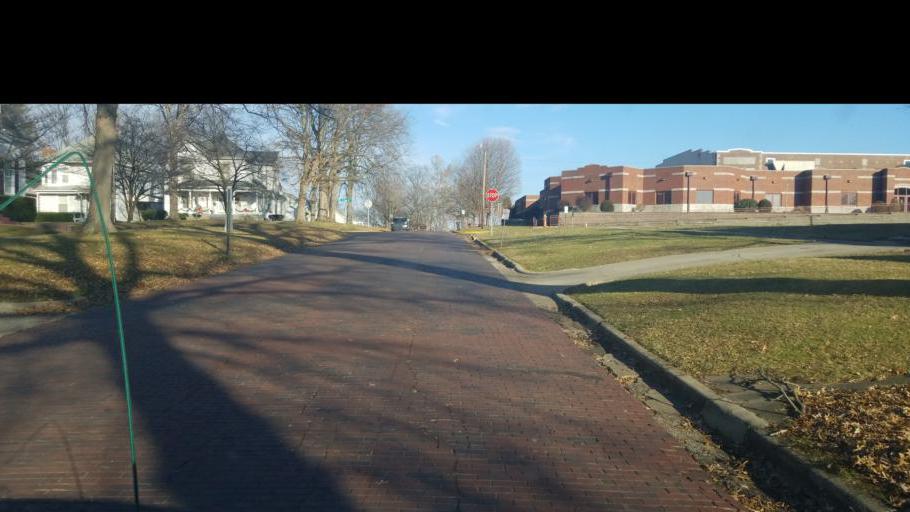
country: US
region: Illinois
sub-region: Wabash County
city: Mount Carmel
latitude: 38.4098
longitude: -87.7561
